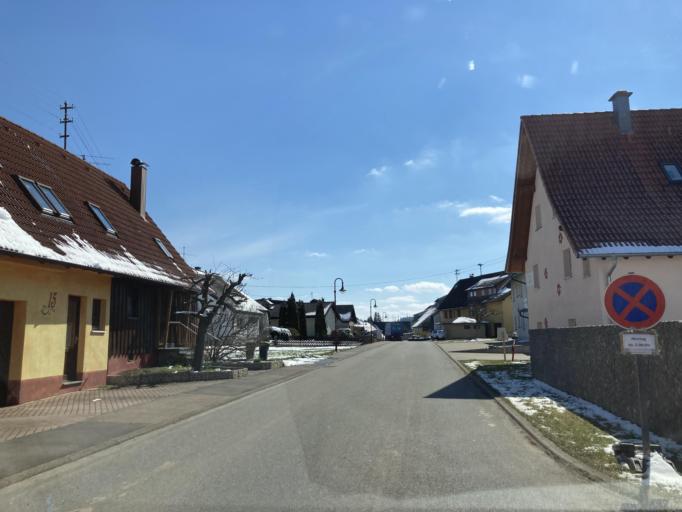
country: DE
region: Baden-Wuerttemberg
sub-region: Freiburg Region
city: Seedorf
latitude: 48.2655
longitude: 8.4822
